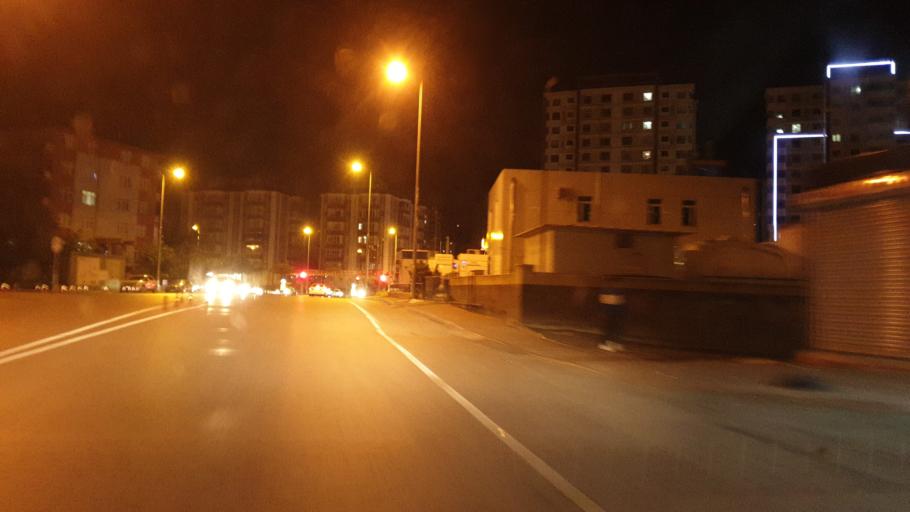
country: TR
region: Kayseri
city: Talas
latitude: 38.6950
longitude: 35.5458
